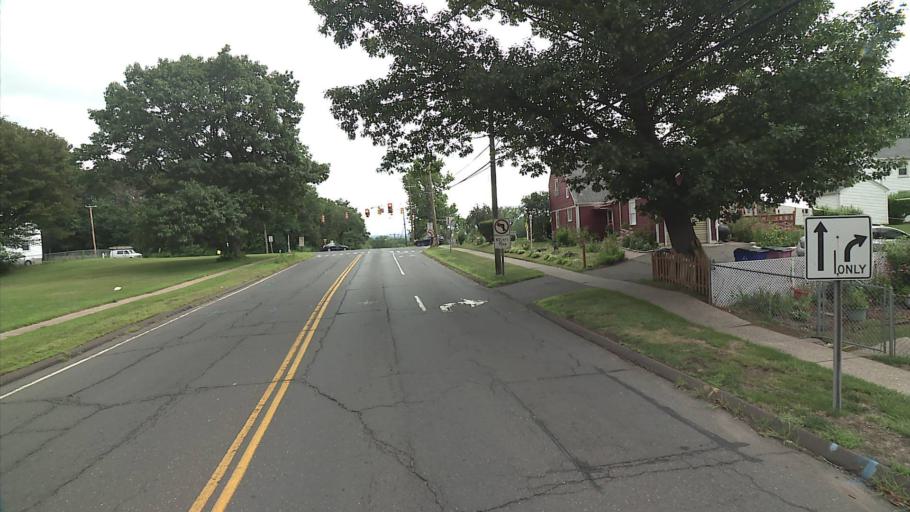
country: US
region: Connecticut
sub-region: Hartford County
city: Newington
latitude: 41.7203
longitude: -72.6924
